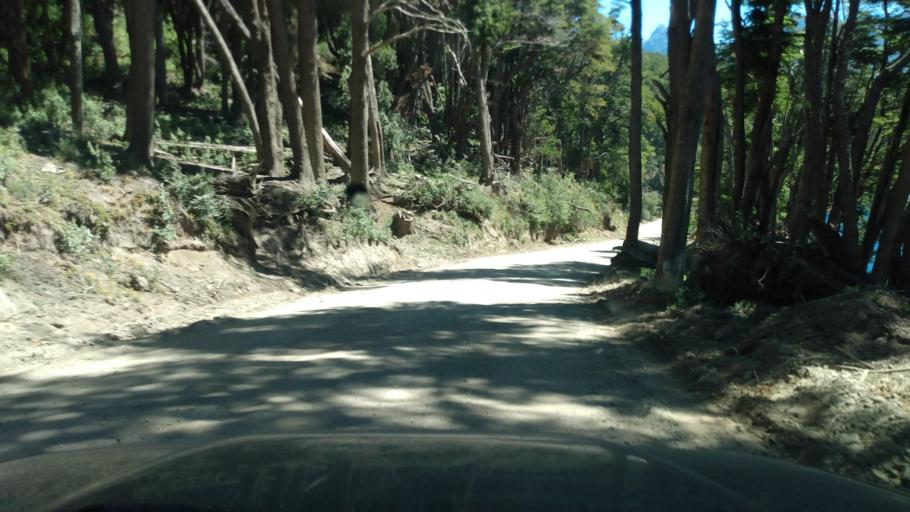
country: AR
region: Neuquen
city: Villa La Angostura
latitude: -40.6159
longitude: -71.5410
